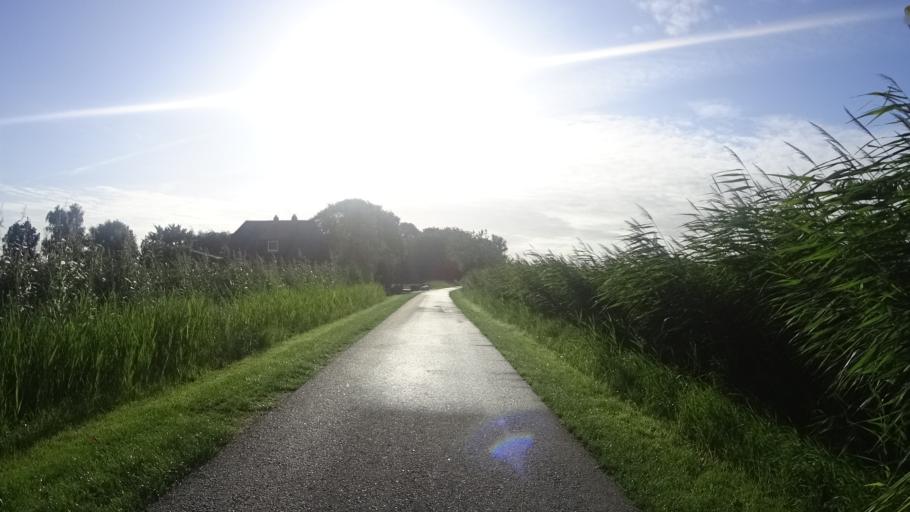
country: DE
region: Lower Saxony
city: Nordenham
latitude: 53.4969
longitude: 8.4304
